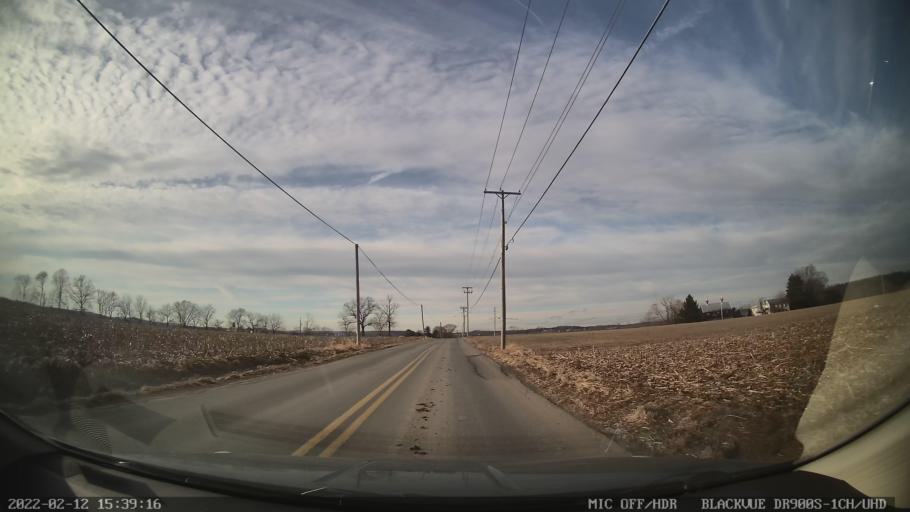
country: US
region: Pennsylvania
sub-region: Berks County
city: Kutztown
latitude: 40.5108
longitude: -75.7400
